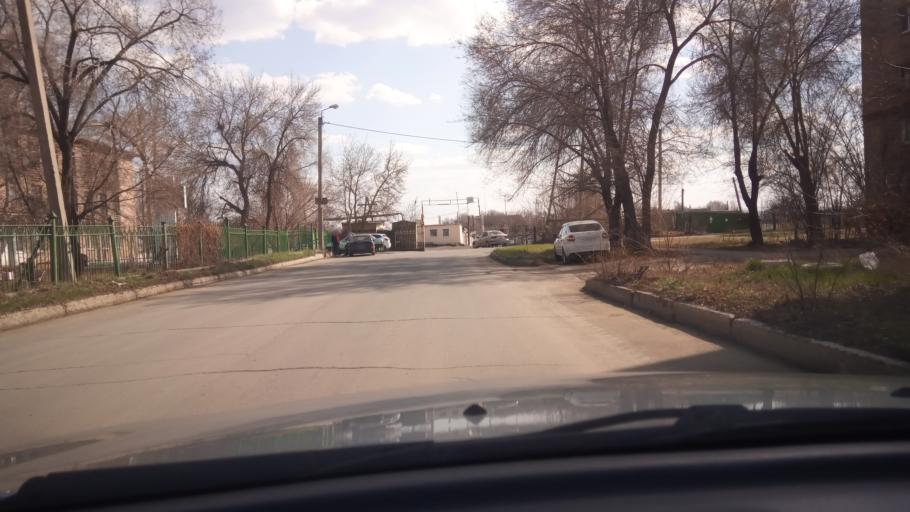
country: RU
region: Orenburg
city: Novotroitsk
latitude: 51.1948
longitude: 58.3143
